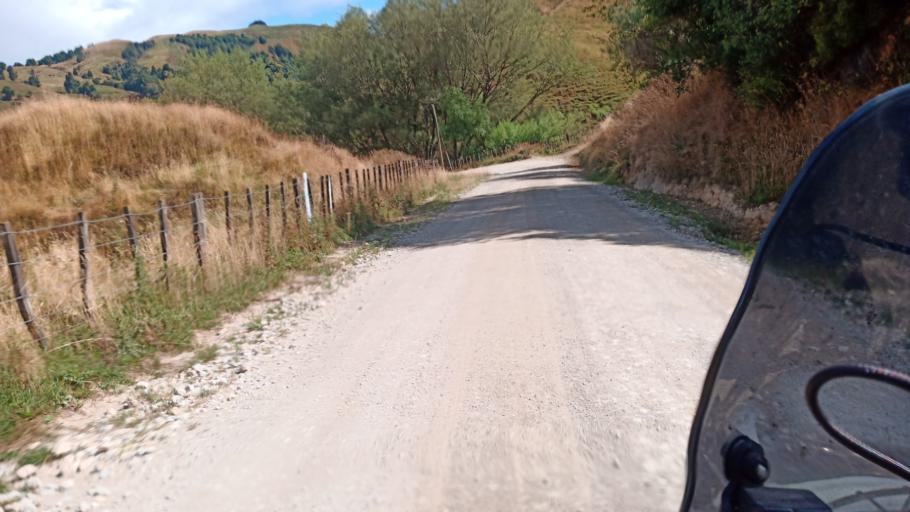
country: NZ
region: Hawke's Bay
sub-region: Wairoa District
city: Wairoa
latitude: -38.6064
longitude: 177.4557
